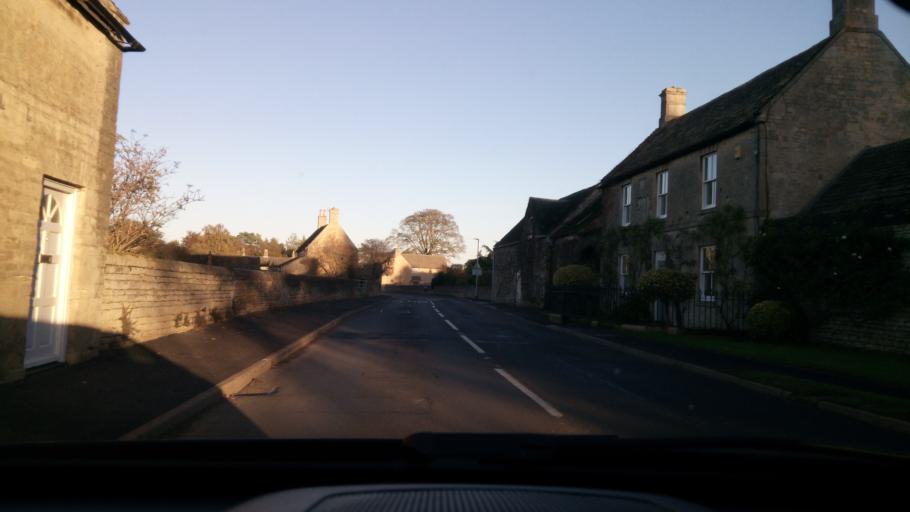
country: GB
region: England
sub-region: Peterborough
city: Barnack
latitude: 52.6344
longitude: -0.4049
